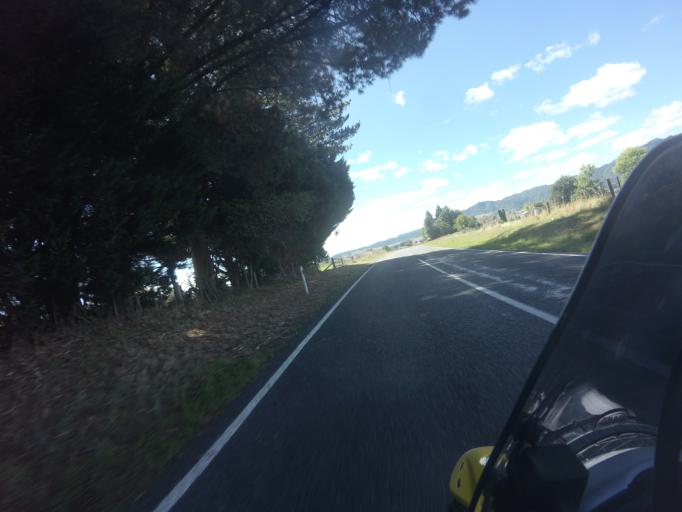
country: NZ
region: Bay of Plenty
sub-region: Whakatane District
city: Murupara
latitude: -38.3481
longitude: 176.7837
